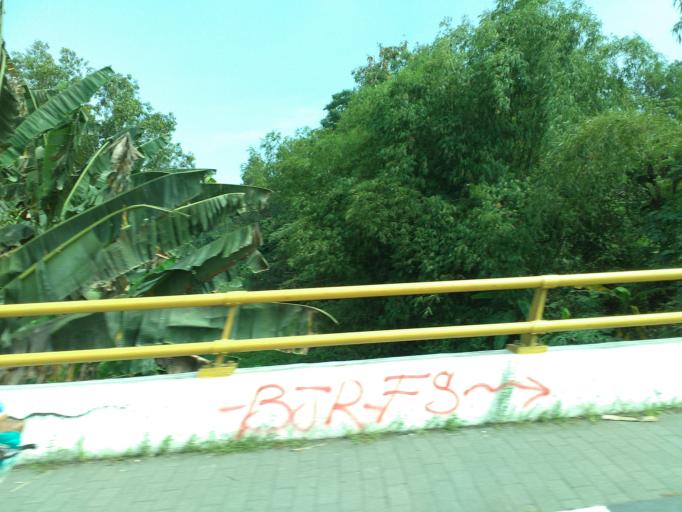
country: ID
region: Central Java
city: Candi Prambanan
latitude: -7.7544
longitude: 110.5110
